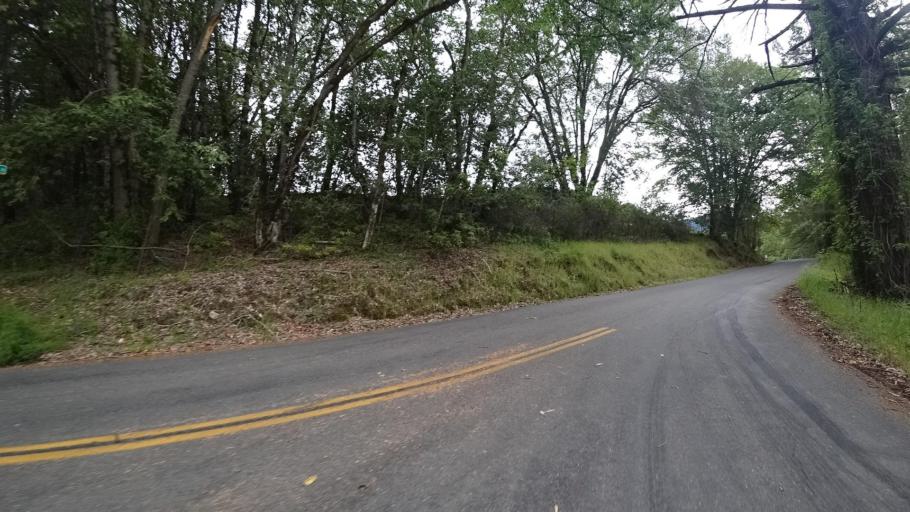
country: US
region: California
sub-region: Humboldt County
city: Willow Creek
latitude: 40.9476
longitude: -123.6255
